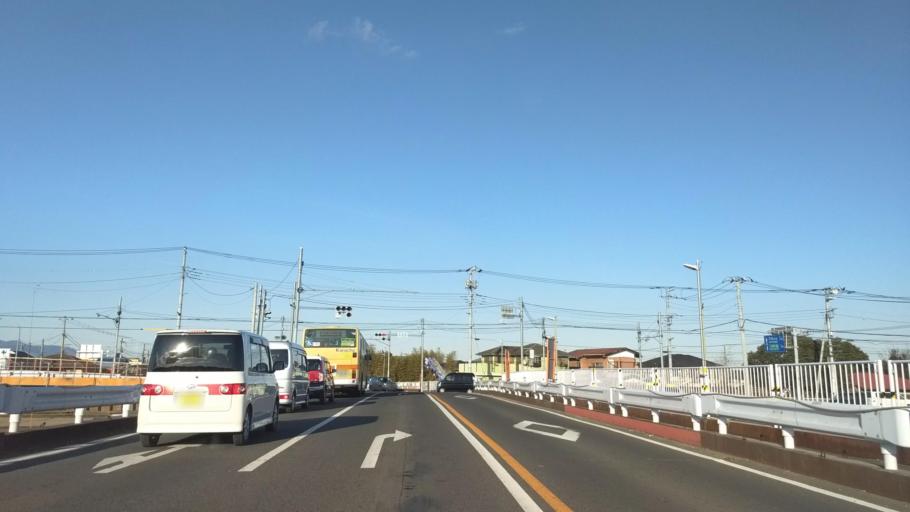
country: JP
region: Kanagawa
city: Isehara
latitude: 35.3589
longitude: 139.2981
